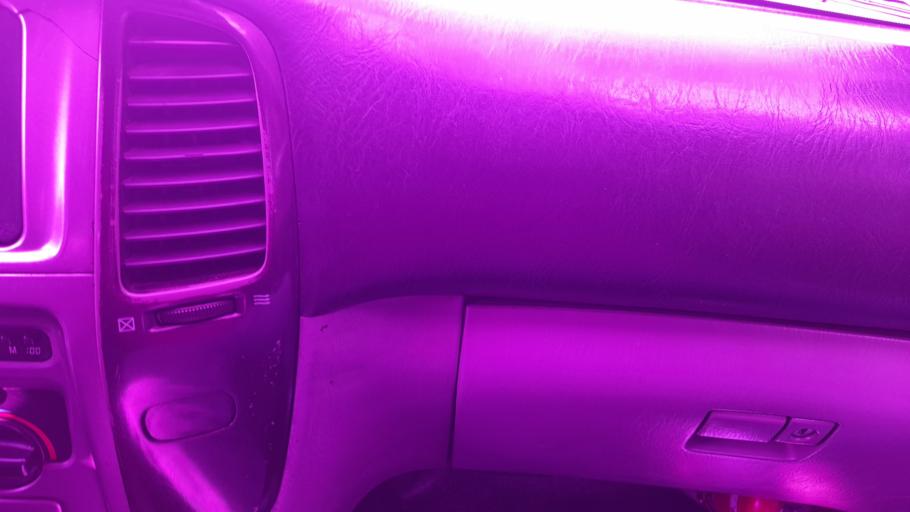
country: ET
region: Oromiya
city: Jima
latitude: 7.5123
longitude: 36.5248
